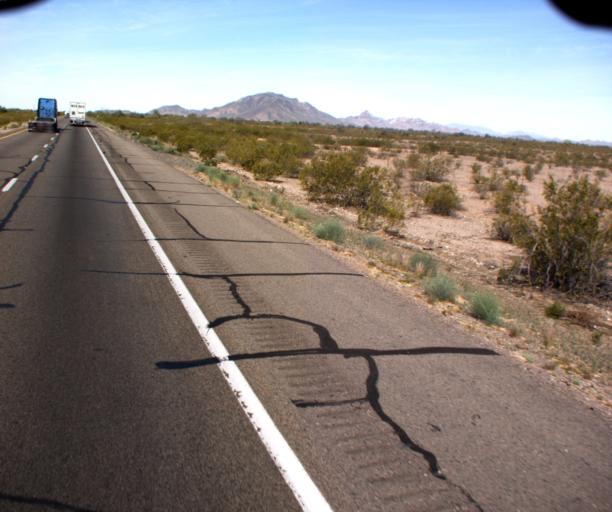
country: US
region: Arizona
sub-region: Maricopa County
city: Buckeye
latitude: 33.5069
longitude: -112.9874
